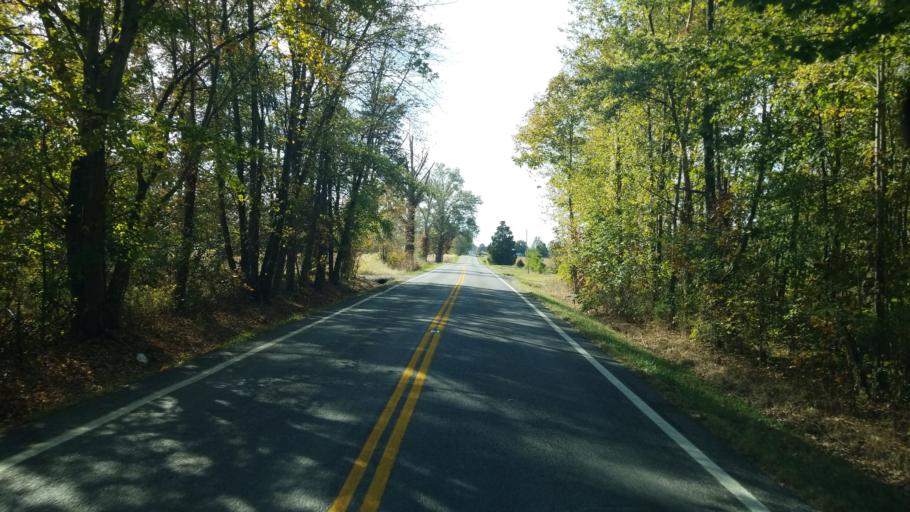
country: US
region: Ohio
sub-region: Warren County
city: Morrow
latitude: 39.4063
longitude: -84.0247
